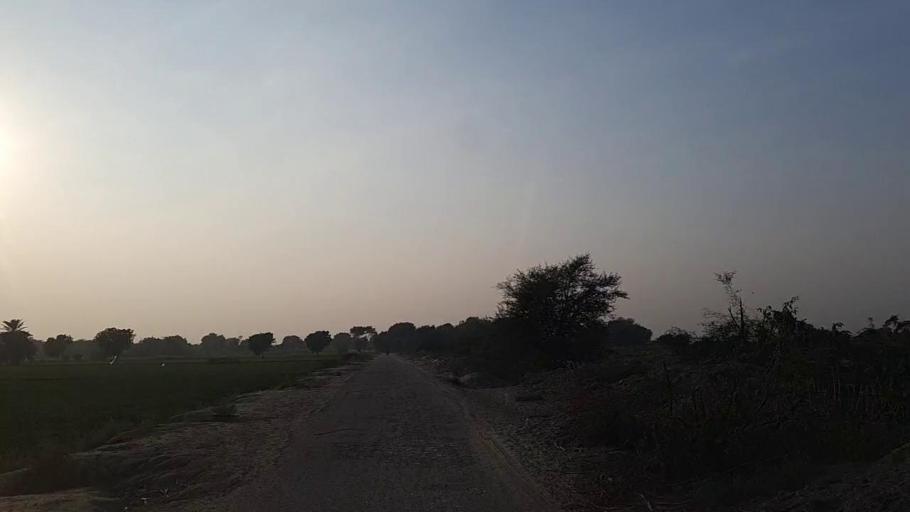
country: PK
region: Sindh
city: Jam Sahib
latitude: 26.4314
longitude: 68.5900
